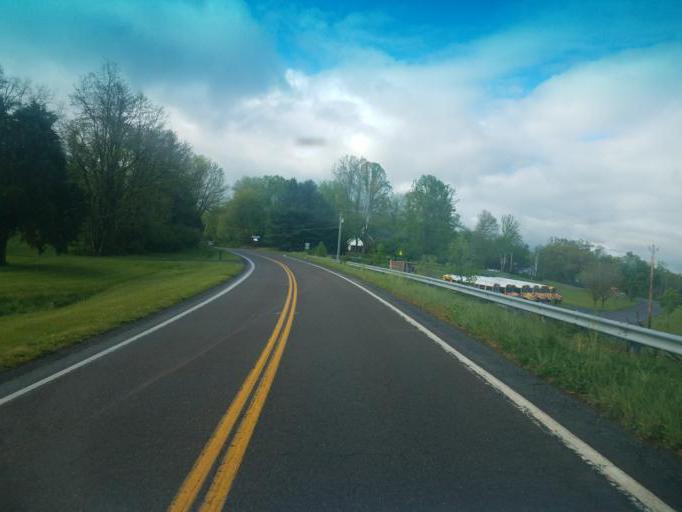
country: US
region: Virginia
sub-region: Washington County
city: Emory
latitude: 36.6834
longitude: -81.8151
